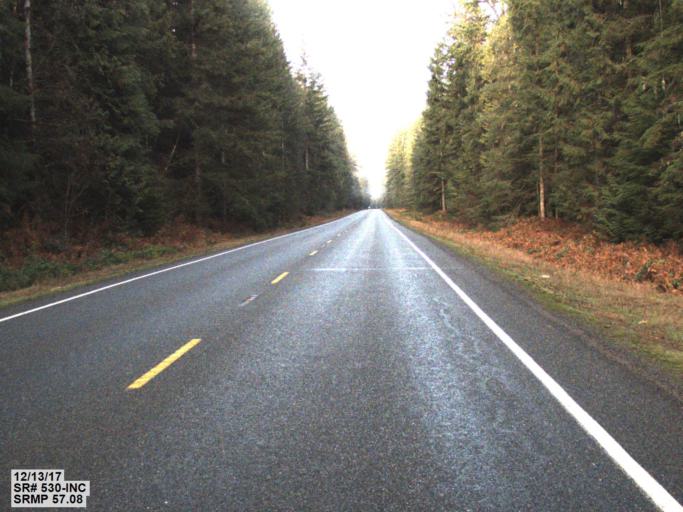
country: US
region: Washington
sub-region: Snohomish County
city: Darrington
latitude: 48.3517
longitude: -121.5399
